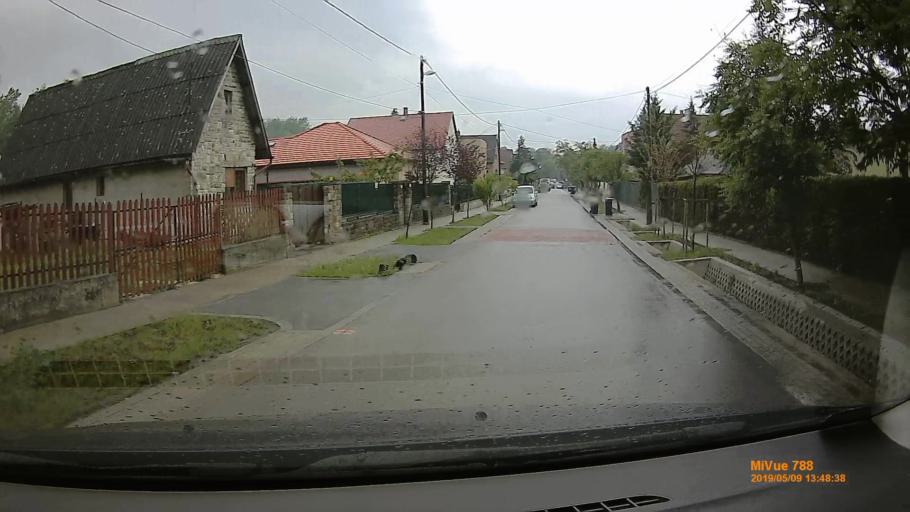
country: HU
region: Budapest
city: Budapest XVI. keruelet
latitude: 47.5308
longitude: 19.1907
